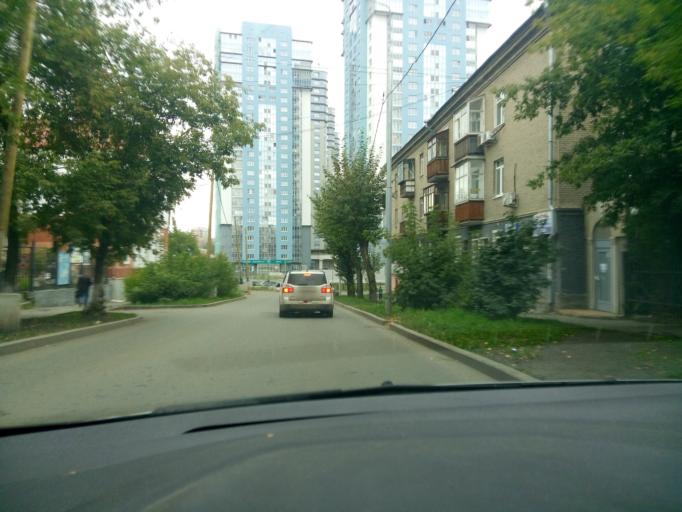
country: RU
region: Sverdlovsk
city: Yekaterinburg
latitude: 56.8412
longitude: 60.5706
